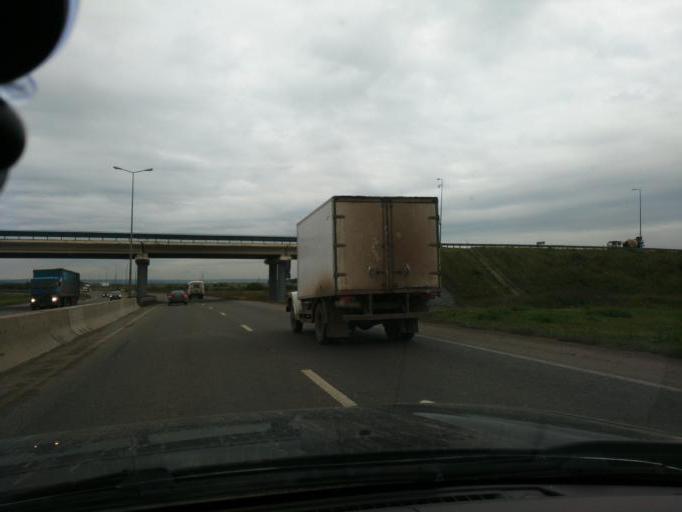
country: RU
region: Perm
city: Kondratovo
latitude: 57.9295
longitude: 56.1716
